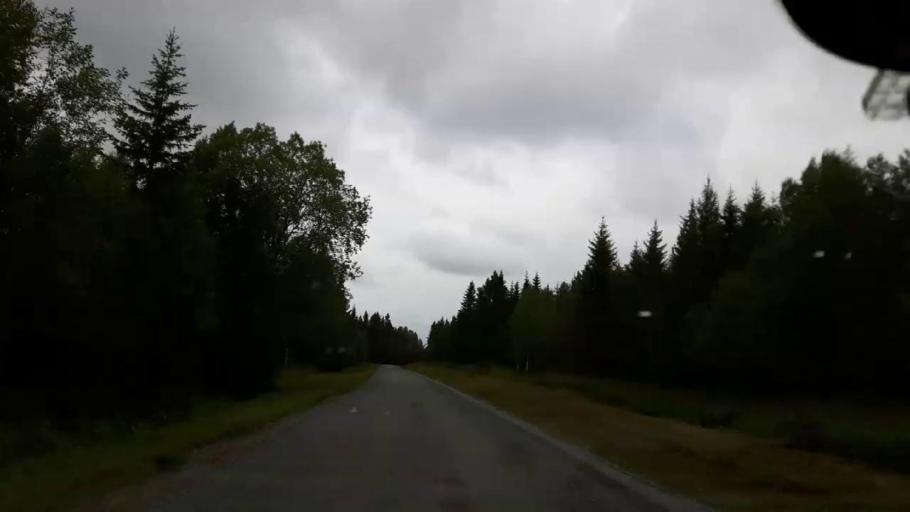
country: SE
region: Jaemtland
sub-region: OEstersunds Kommun
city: Ostersund
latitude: 63.0684
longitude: 14.5530
